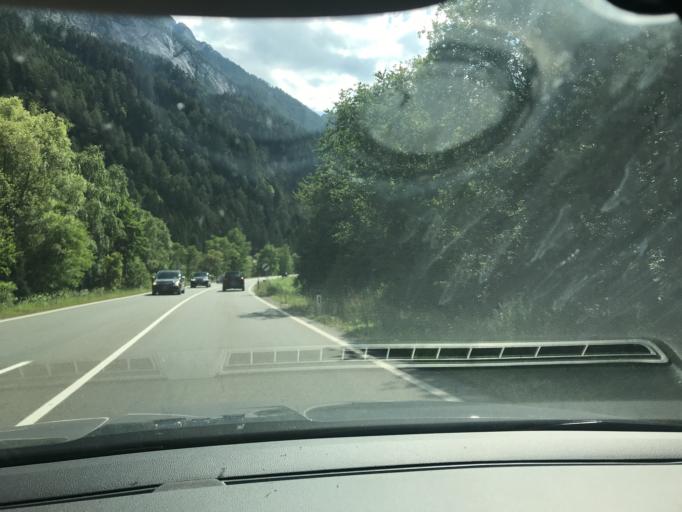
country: AT
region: Tyrol
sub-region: Politischer Bezirk Lienz
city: Leisach
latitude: 46.7963
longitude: 12.7338
